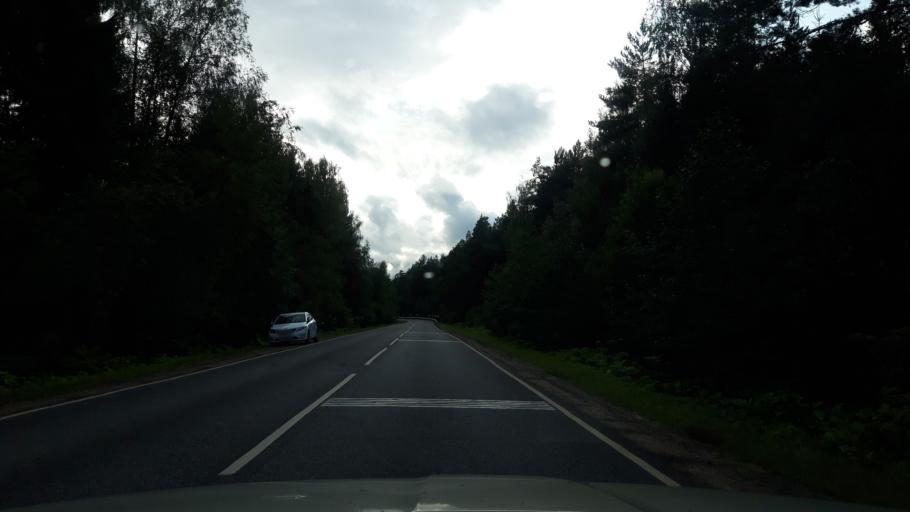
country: RU
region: Moskovskaya
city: Solnechnogorsk
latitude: 56.0958
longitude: 36.8811
